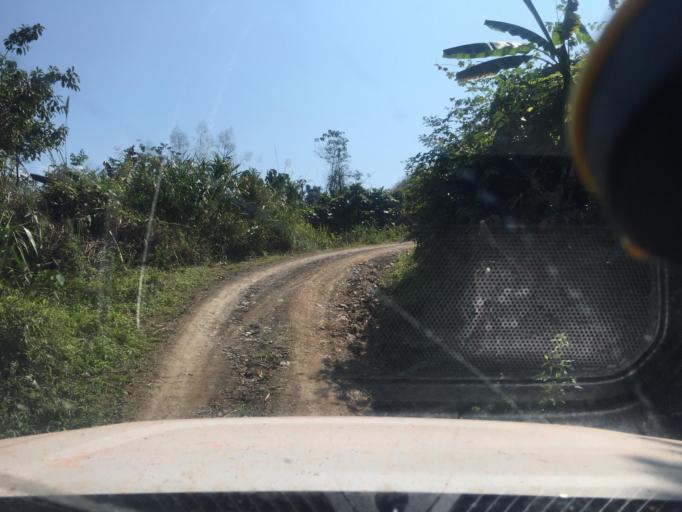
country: LA
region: Phongsali
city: Phongsali
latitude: 21.6561
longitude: 102.4146
